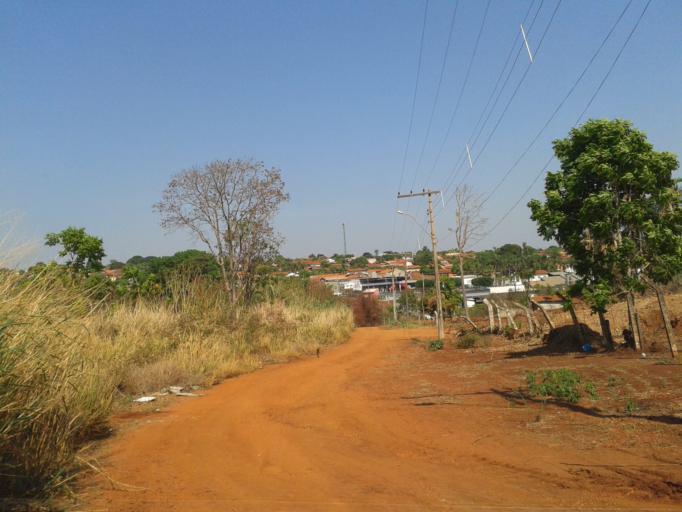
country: BR
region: Minas Gerais
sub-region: Ituiutaba
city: Ituiutaba
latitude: -18.9524
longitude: -49.4542
